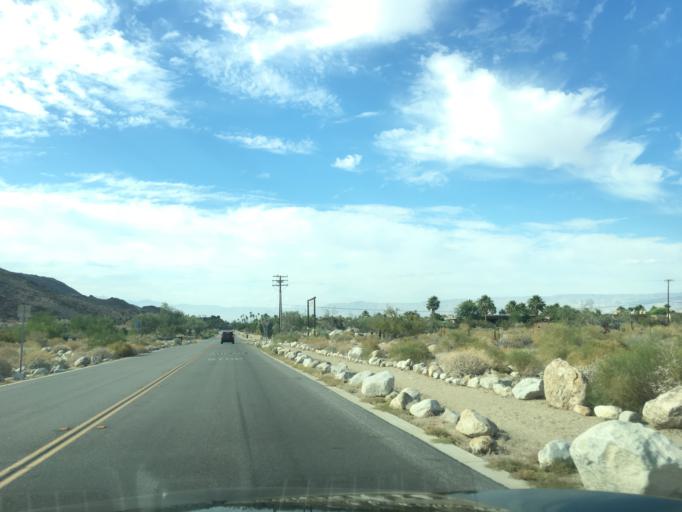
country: US
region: California
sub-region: Riverside County
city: Palm Springs
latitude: 33.7710
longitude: -116.5456
